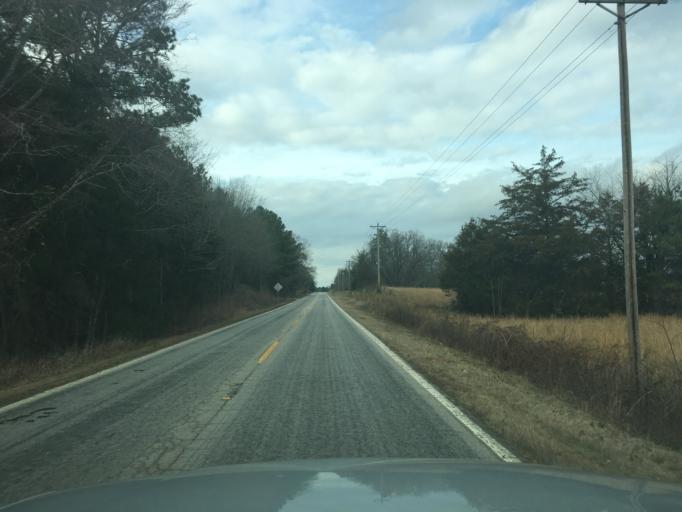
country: US
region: South Carolina
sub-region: Abbeville County
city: Due West
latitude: 34.3042
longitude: -82.4546
